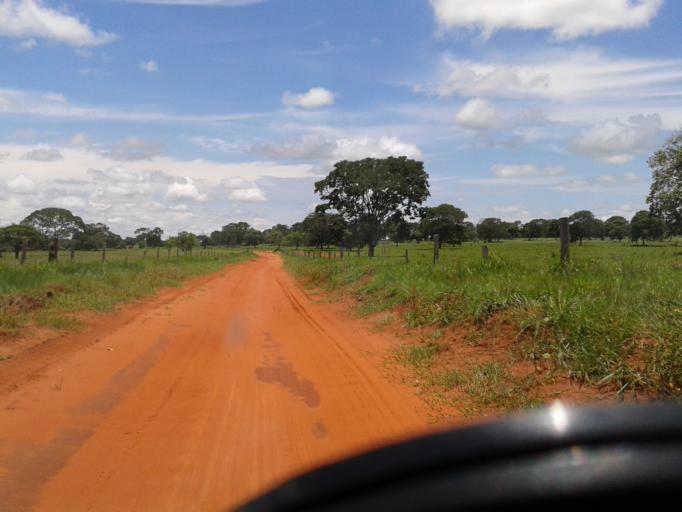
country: BR
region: Minas Gerais
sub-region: Santa Vitoria
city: Santa Vitoria
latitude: -18.9573
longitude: -49.8646
